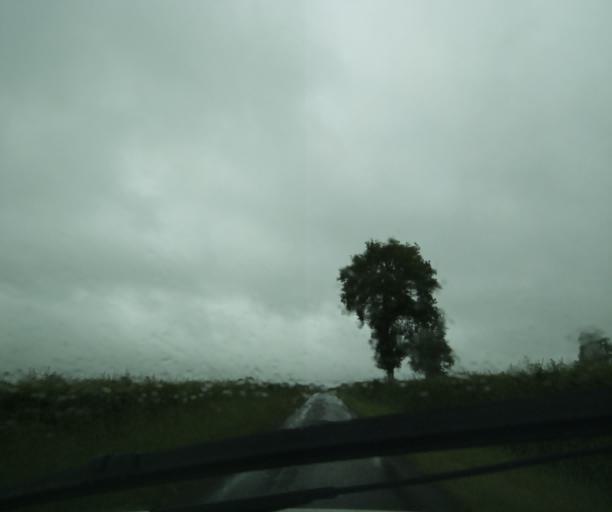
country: FR
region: Bourgogne
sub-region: Departement de Saone-et-Loire
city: Ciry-le-Noble
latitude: 46.5435
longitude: 4.3697
